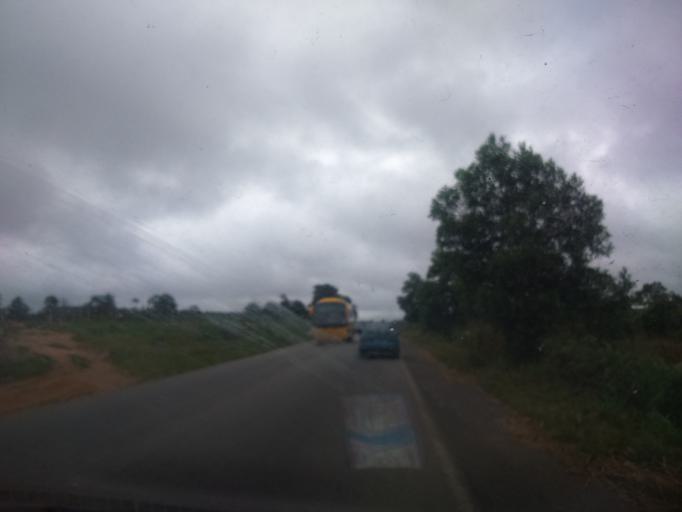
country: CI
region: Sud-Comoe
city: Bonoua
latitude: 5.2789
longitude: -3.5494
